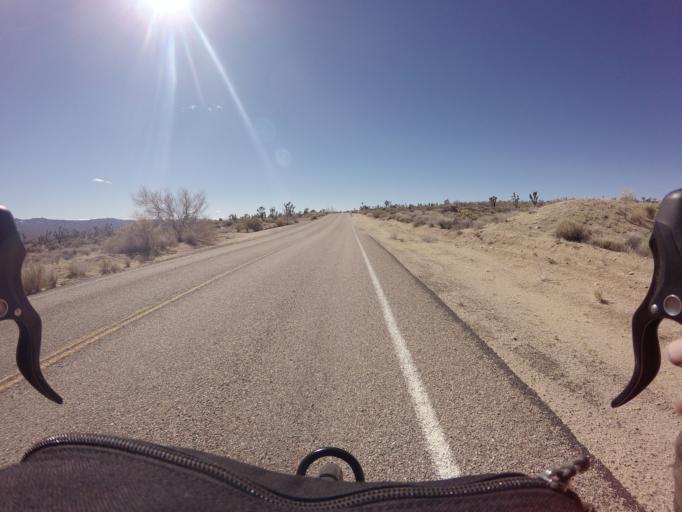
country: US
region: Nevada
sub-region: Clark County
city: Sandy Valley
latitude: 35.2889
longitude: -115.4959
